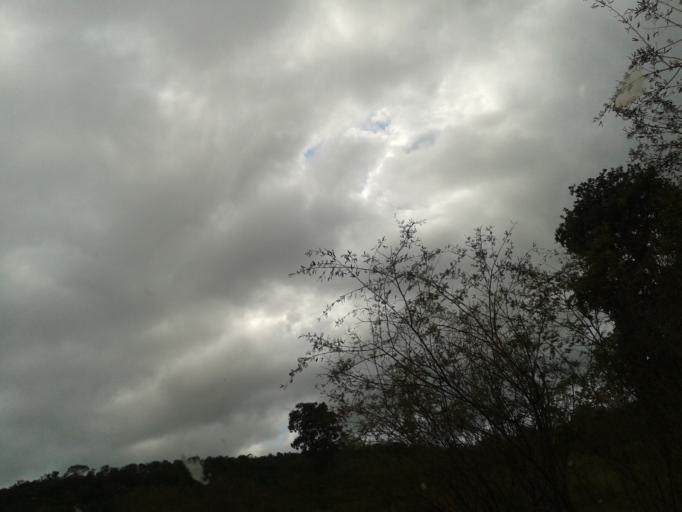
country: BR
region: Minas Gerais
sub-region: Campina Verde
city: Campina Verde
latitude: -19.4615
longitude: -49.5893
